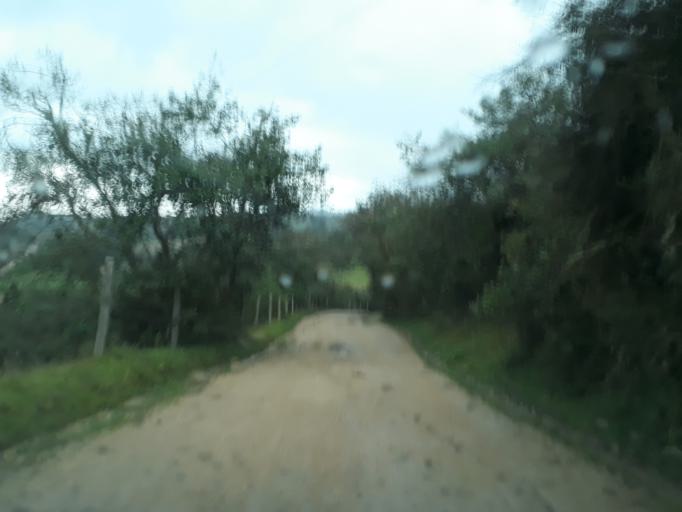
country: CO
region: Cundinamarca
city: Villapinzon
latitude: 5.2947
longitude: -73.6165
